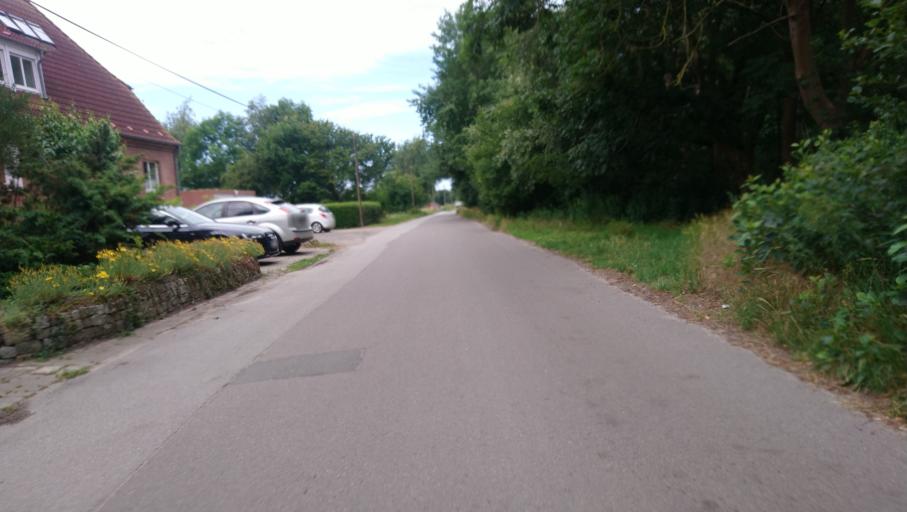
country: DE
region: Mecklenburg-Vorpommern
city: Elmenhorst
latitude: 54.1725
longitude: 12.0138
